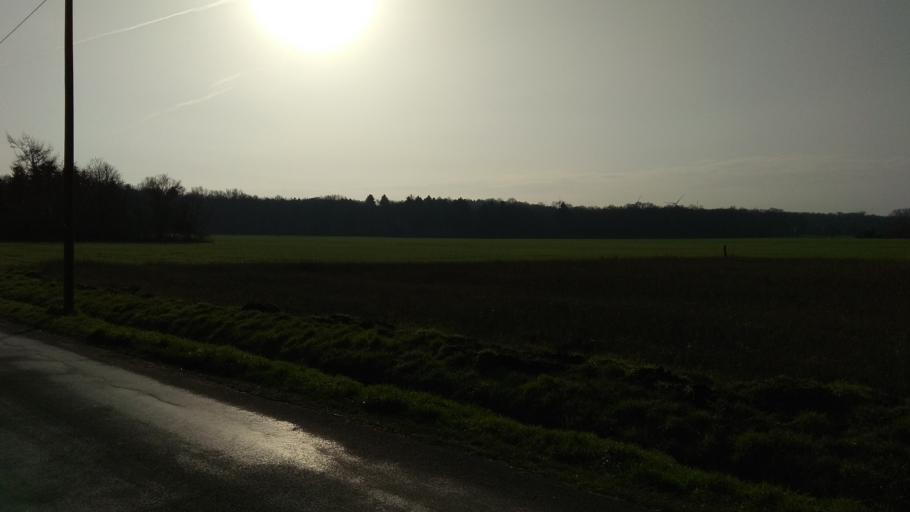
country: DE
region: North Rhine-Westphalia
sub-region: Regierungsbezirk Dusseldorf
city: Hunxe
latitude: 51.6475
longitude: 6.7971
